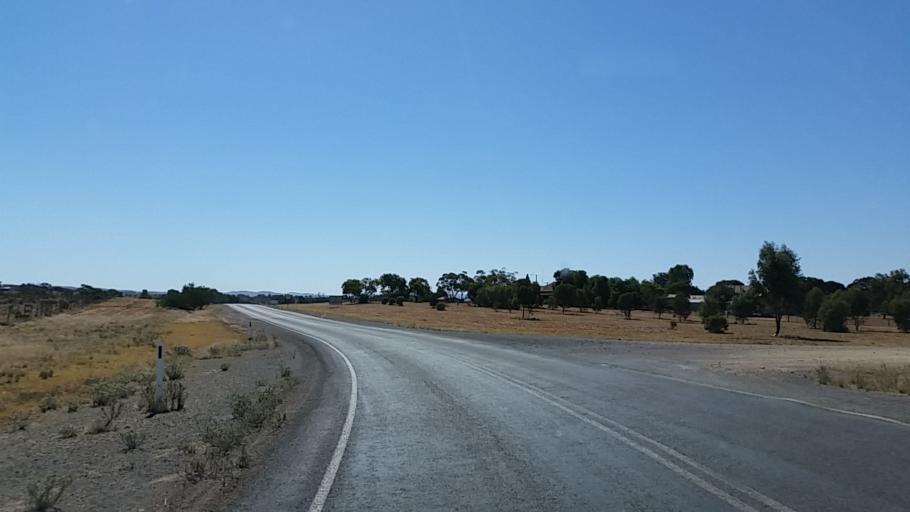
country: AU
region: South Australia
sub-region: Peterborough
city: Peterborough
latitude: -32.7284
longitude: 138.6154
